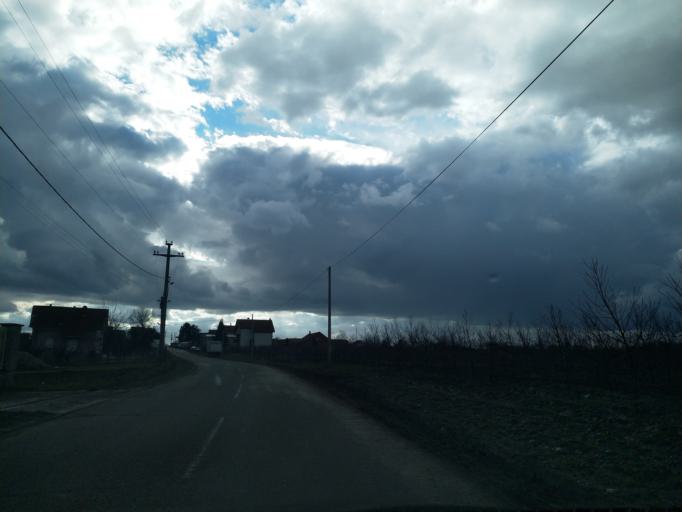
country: RS
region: Central Serbia
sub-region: Belgrade
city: Grocka
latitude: 44.6180
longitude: 20.7313
